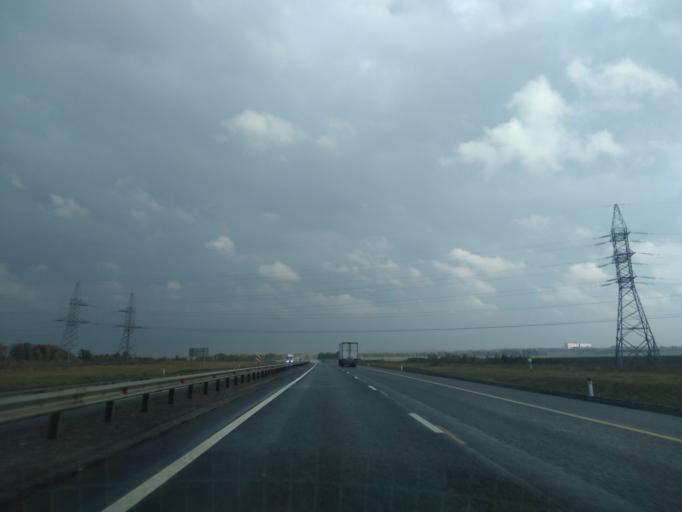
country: RU
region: Lipetsk
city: Yelets
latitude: 52.5855
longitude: 38.6826
